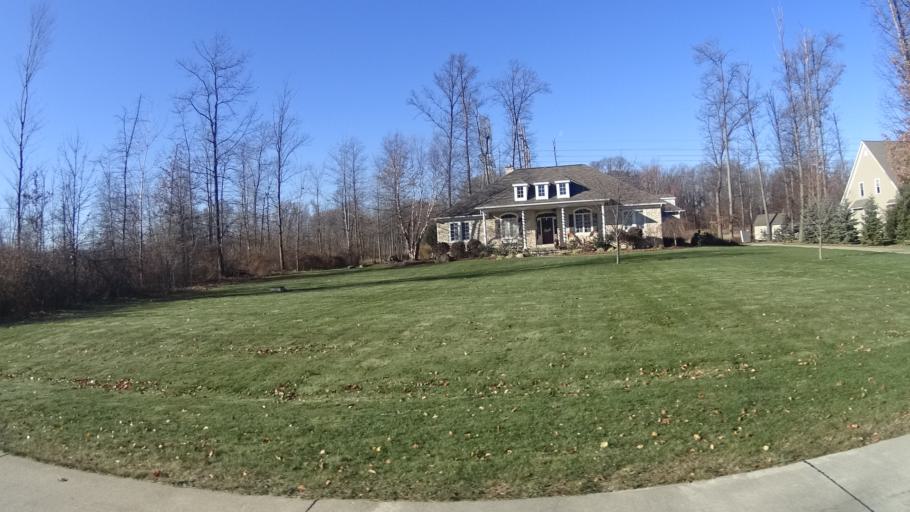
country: US
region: Ohio
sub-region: Lorain County
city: South Amherst
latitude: 41.3871
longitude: -82.2668
